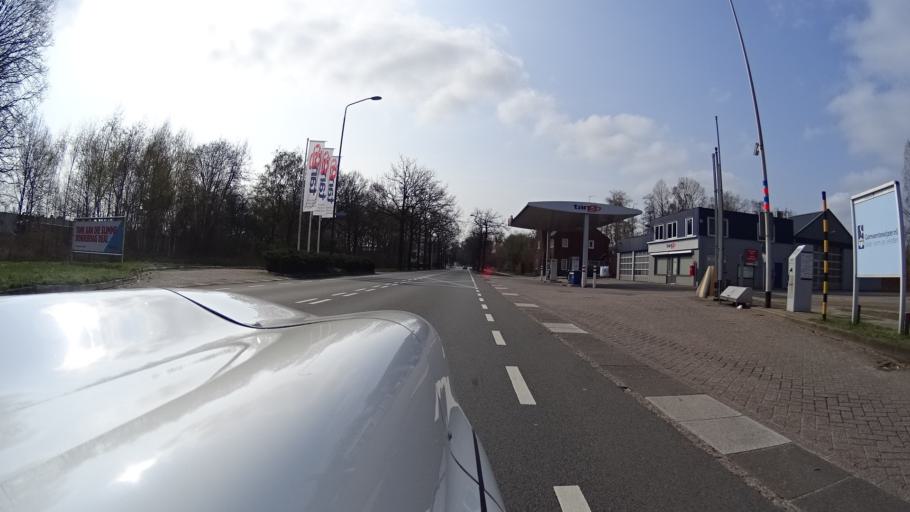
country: NL
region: North Brabant
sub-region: Gemeente Laarbeek
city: Aarle-Rixtel
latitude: 51.5215
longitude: 5.6404
